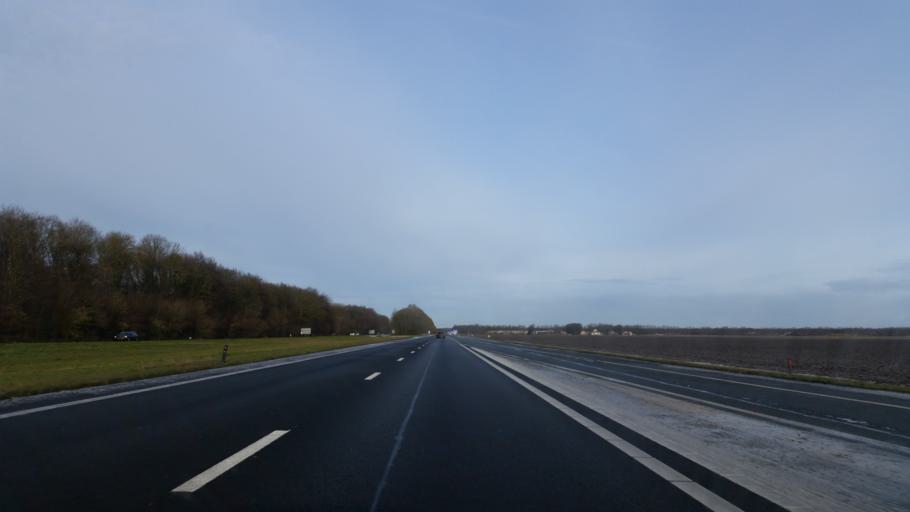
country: NL
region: Flevoland
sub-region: Gemeente Noordoostpolder
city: Emmeloord
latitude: 52.7697
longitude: 5.7631
